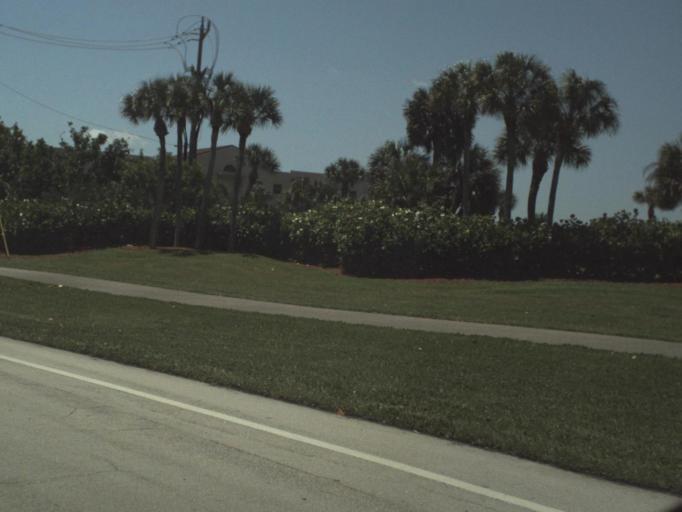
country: US
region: Florida
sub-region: Brevard County
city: Micco
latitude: 27.9207
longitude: -80.4821
